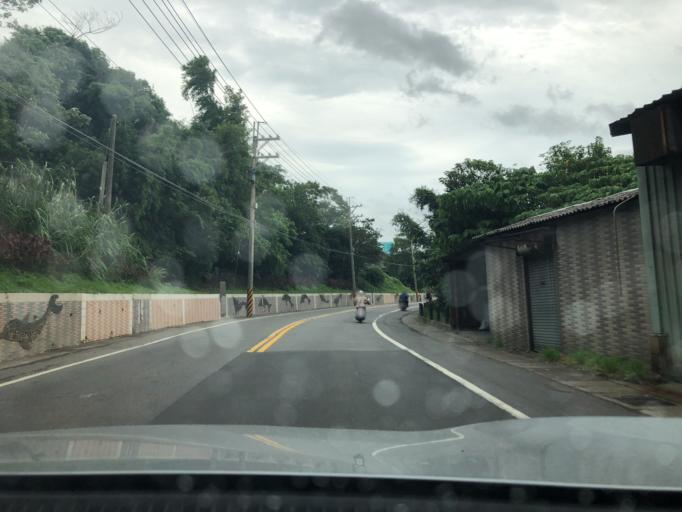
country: TW
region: Taiwan
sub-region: Taoyuan
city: Taoyuan
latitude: 24.9456
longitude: 121.3398
